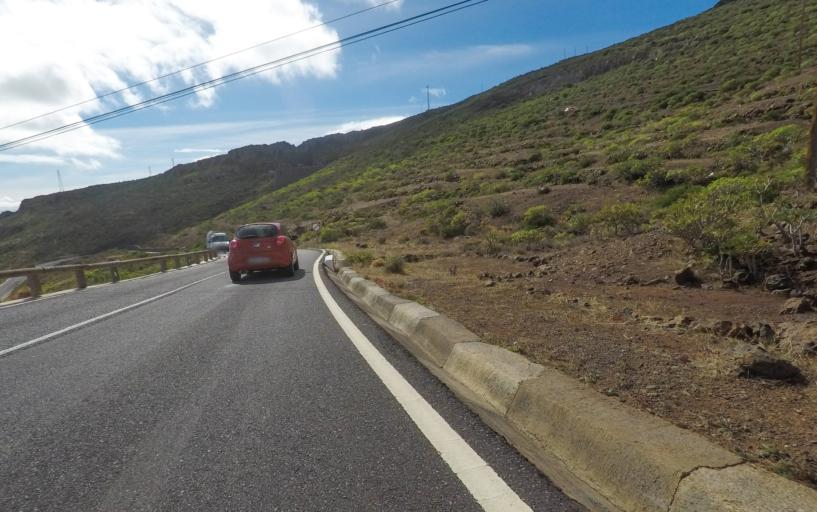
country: ES
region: Canary Islands
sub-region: Provincia de Santa Cruz de Tenerife
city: San Sebastian de la Gomera
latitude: 28.0839
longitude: -17.1290
